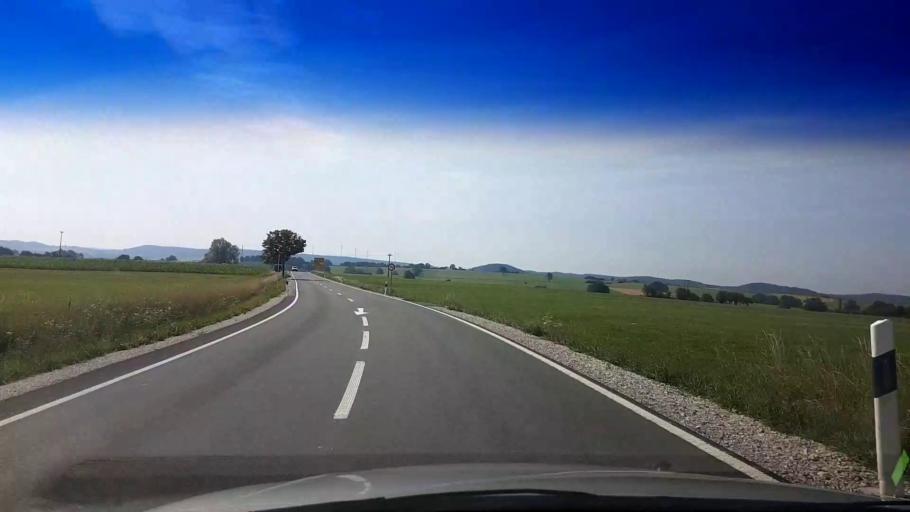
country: DE
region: Bavaria
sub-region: Upper Franconia
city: Mistelgau
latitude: 49.9337
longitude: 11.4724
